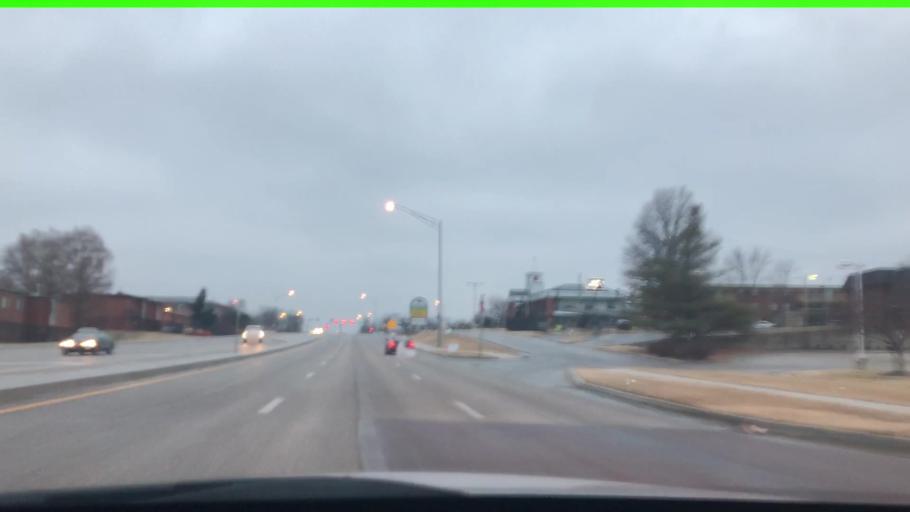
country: US
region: Missouri
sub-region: Boone County
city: Columbia
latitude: 38.9574
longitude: -92.3715
